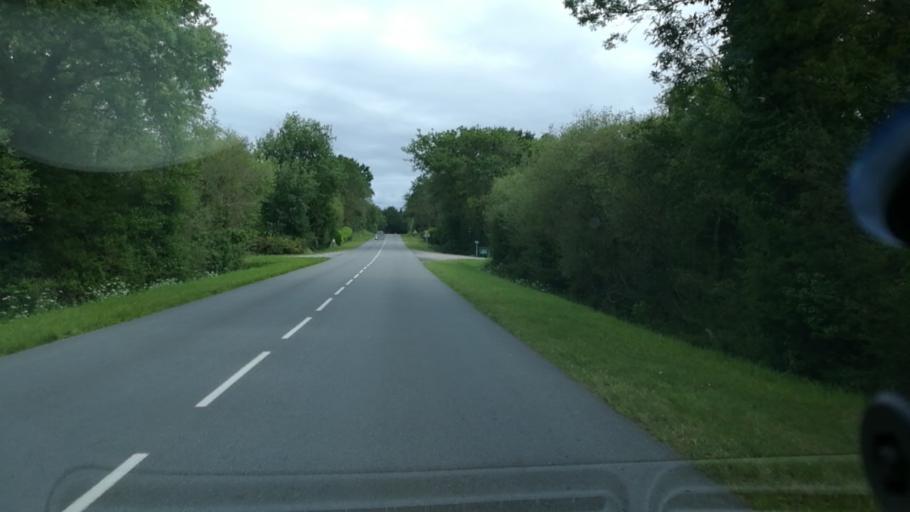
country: FR
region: Brittany
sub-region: Departement du Morbihan
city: Penestin
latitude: 47.4646
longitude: -2.4783
